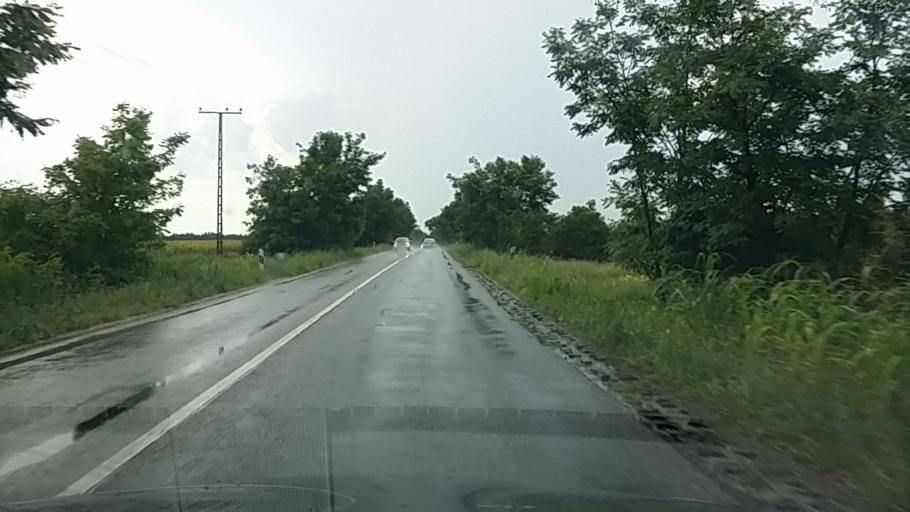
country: HU
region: Pest
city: Felsopakony
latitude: 47.3208
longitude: 19.2956
